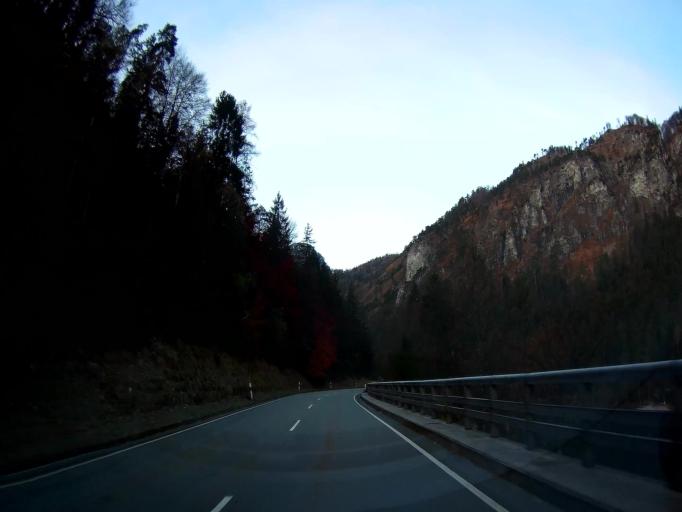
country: DE
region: Bavaria
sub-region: Upper Bavaria
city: Schneizlreuth
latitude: 47.7175
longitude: 12.8224
